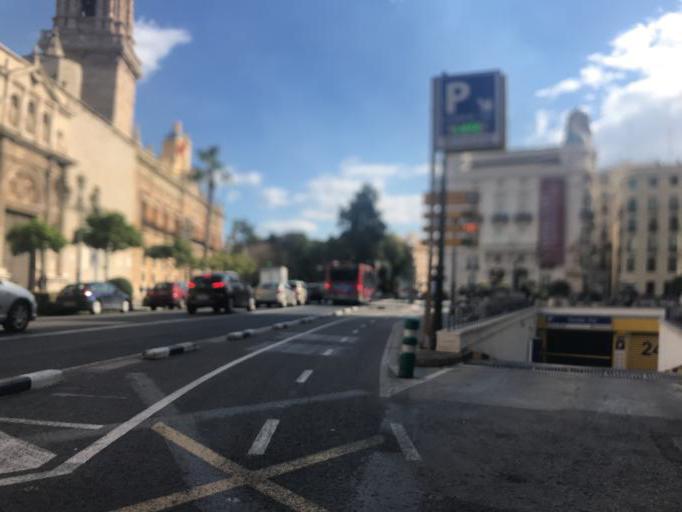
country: ES
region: Valencia
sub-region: Provincia de Valencia
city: Valencia
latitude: 39.4748
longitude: -0.3698
